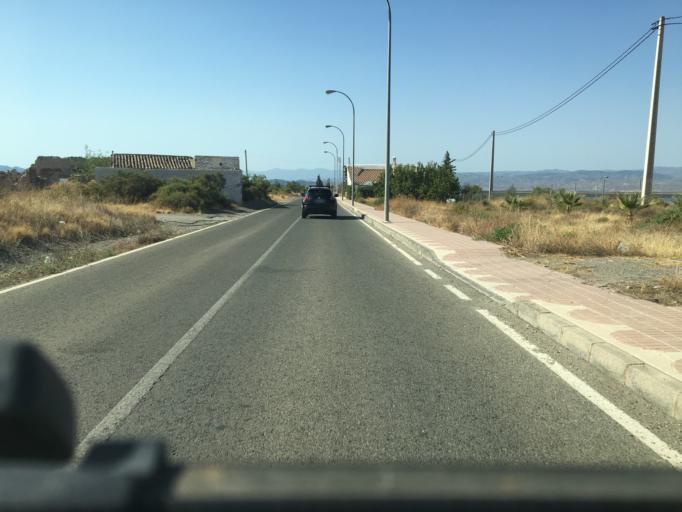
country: ES
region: Andalusia
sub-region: Provincia de Almeria
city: Huercal-Overa
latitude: 37.4567
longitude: -1.9889
